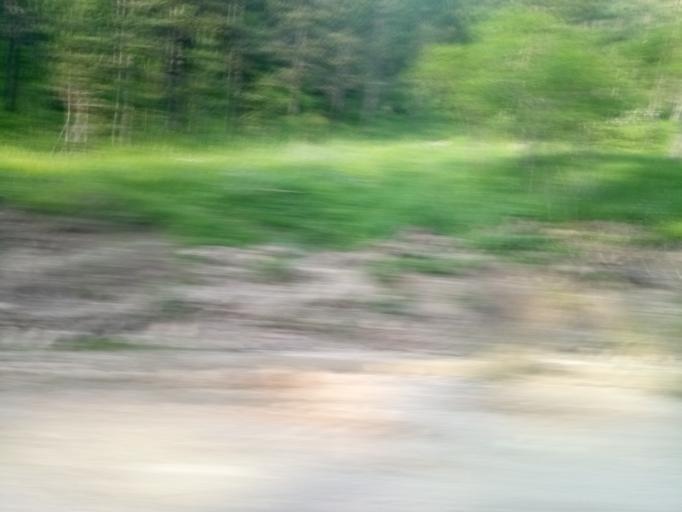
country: TR
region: Karabuk
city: Eskipazar
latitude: 41.0470
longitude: 32.5464
